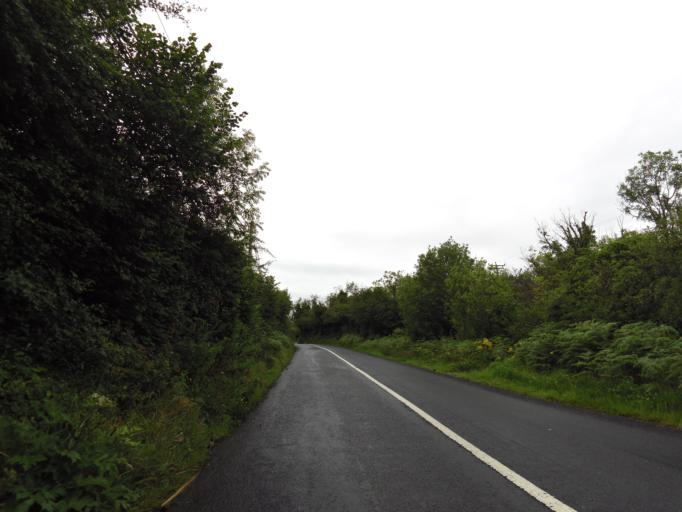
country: IE
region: Connaught
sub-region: County Galway
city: Gaillimh
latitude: 53.2991
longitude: -9.0616
